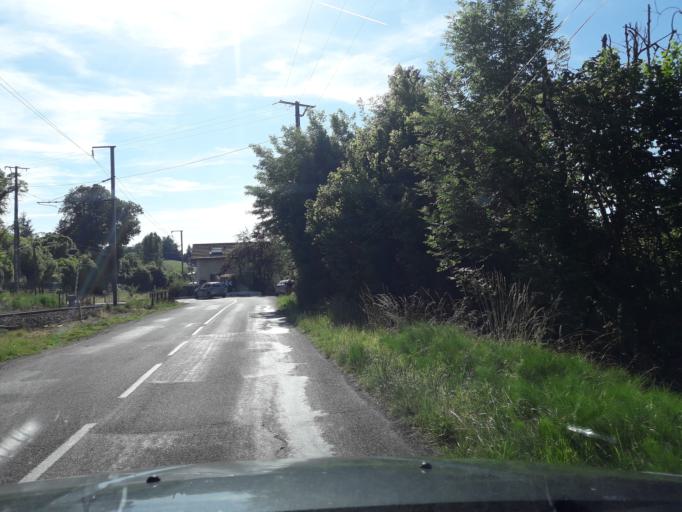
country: FR
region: Rhone-Alpes
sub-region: Departement de la Savoie
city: La Bridoire
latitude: 45.5394
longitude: 5.7850
